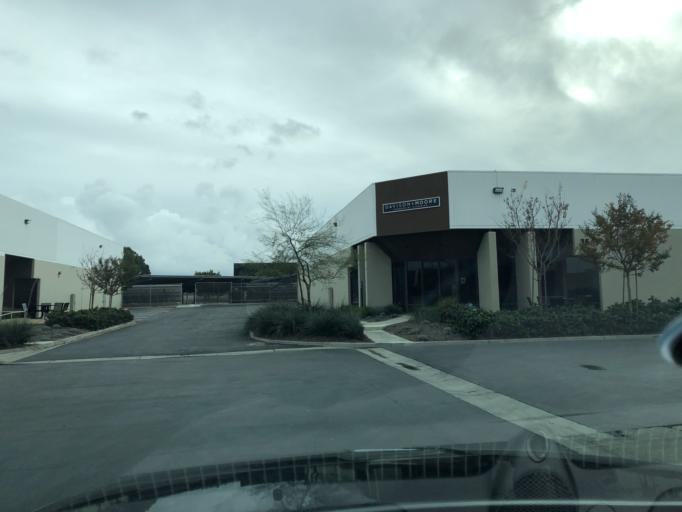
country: US
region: California
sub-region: Orange County
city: Fountain Valley
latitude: 33.6947
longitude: -117.9232
